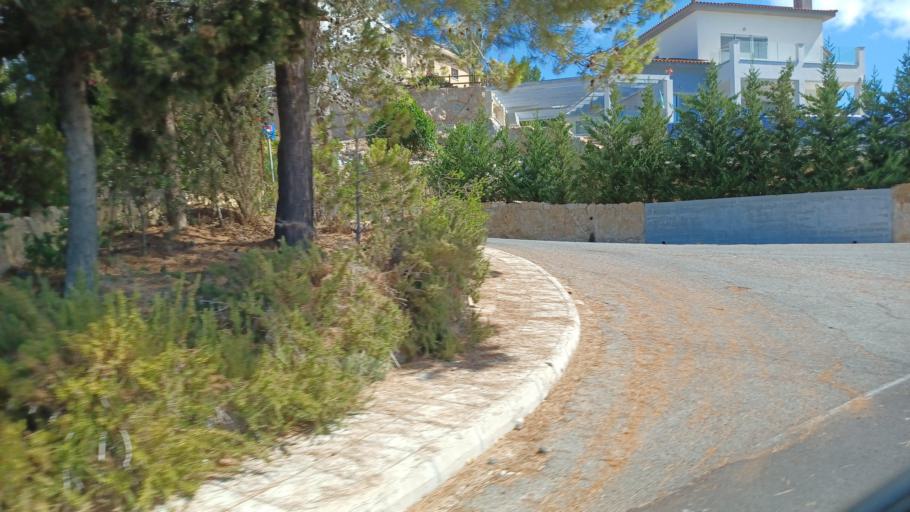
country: CY
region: Pafos
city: Tala
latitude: 34.8509
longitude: 32.4289
